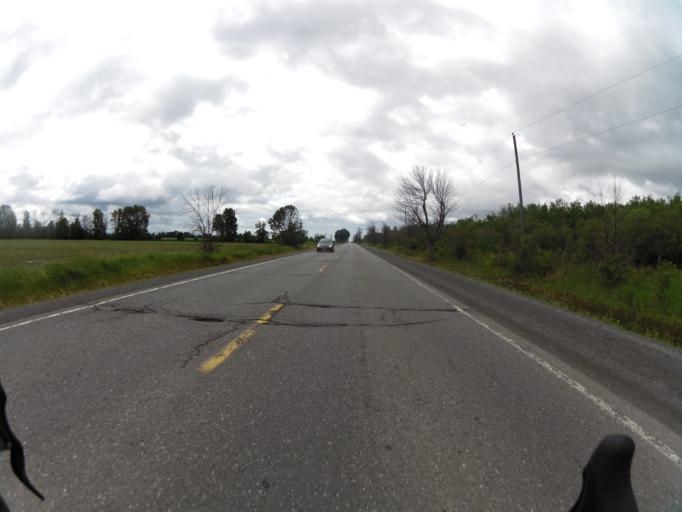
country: CA
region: Ontario
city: Bells Corners
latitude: 45.2644
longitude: -75.8550
